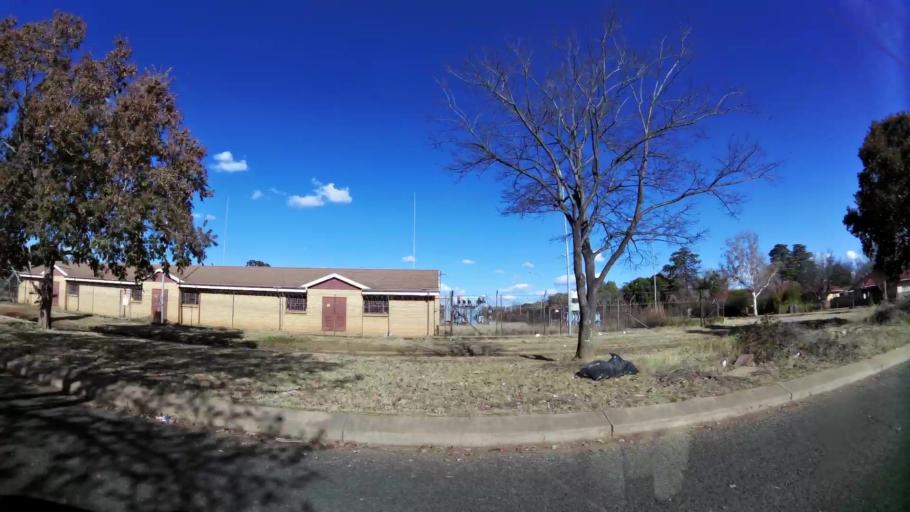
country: ZA
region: Gauteng
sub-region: West Rand District Municipality
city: Carletonville
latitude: -26.3623
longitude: 27.4072
